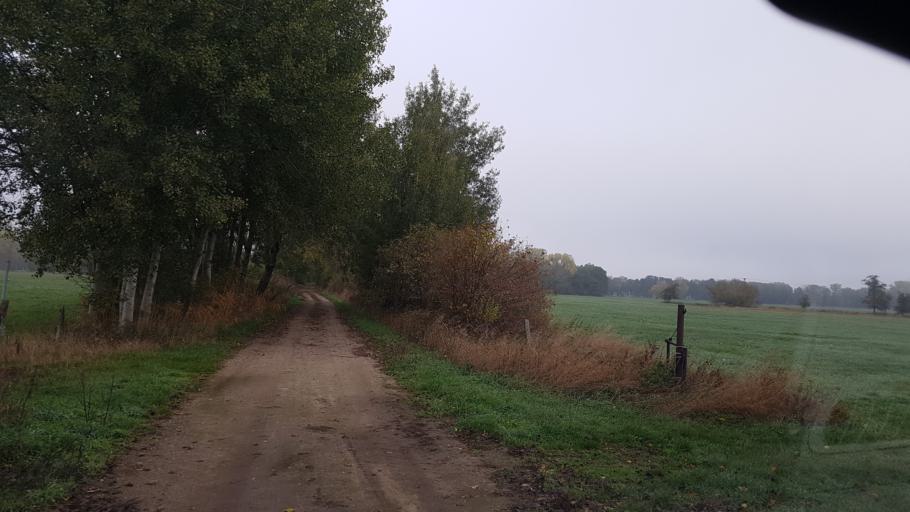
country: DE
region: Brandenburg
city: Schonewalde
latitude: 51.6874
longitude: 13.6012
